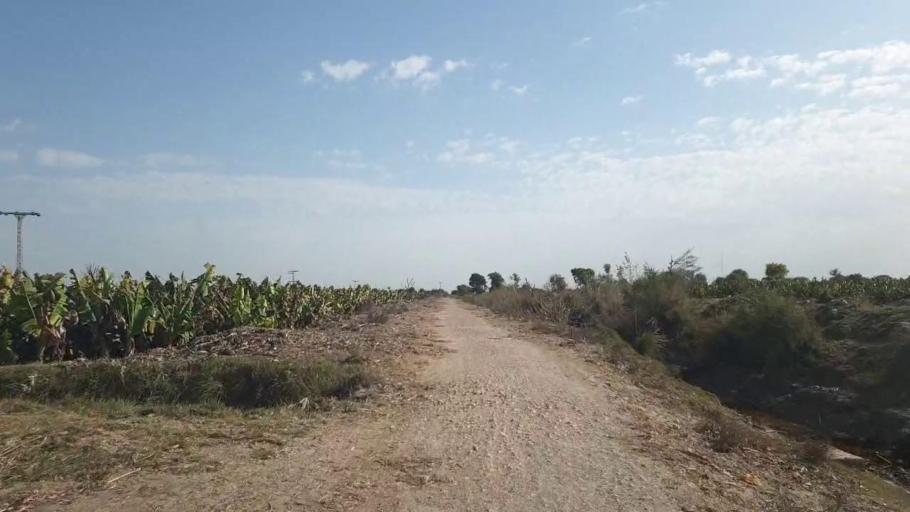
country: PK
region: Sindh
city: Shahdadpur
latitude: 26.0166
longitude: 68.4969
